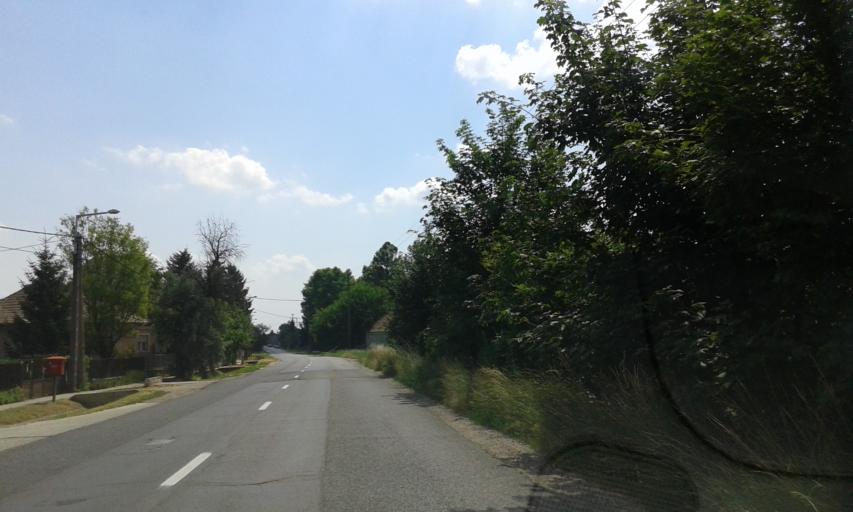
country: HU
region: Fejer
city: Bicske
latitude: 47.4882
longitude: 18.6141
